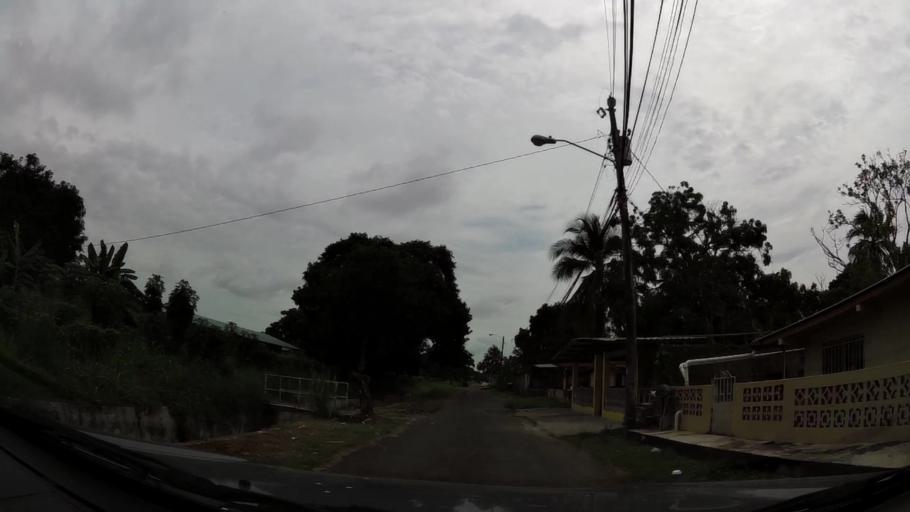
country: PA
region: Panama
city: San Miguelito
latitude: 9.0484
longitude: -79.4300
